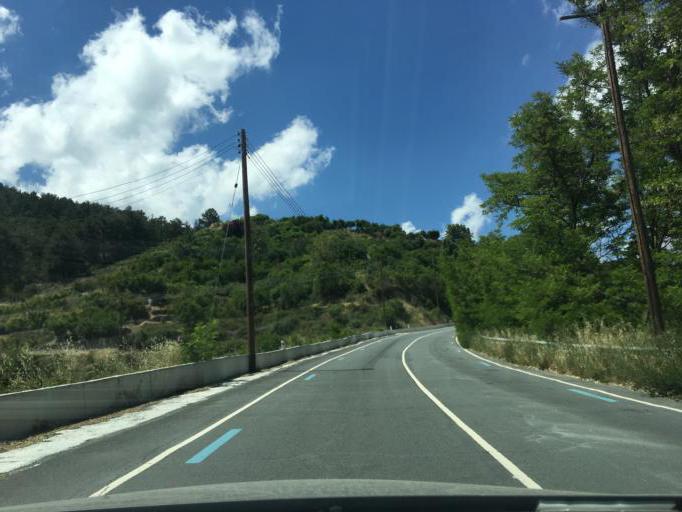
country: CY
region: Limassol
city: Kyperounta
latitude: 34.9337
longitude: 32.9332
